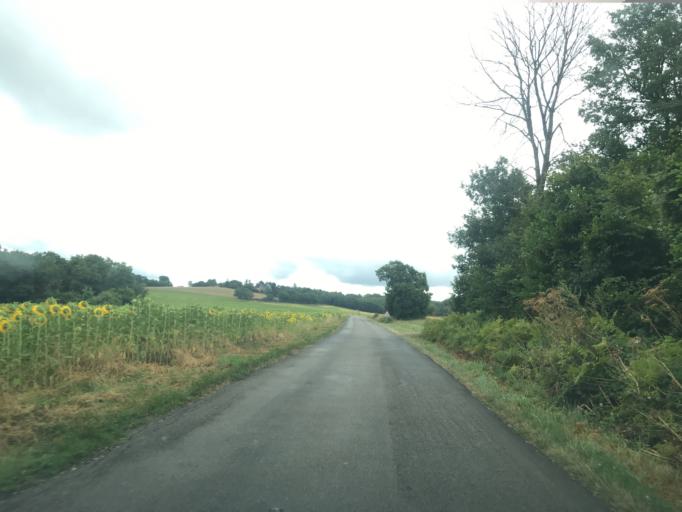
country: FR
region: Poitou-Charentes
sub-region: Departement de la Charente
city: Dignac
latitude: 45.5564
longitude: 0.2525
